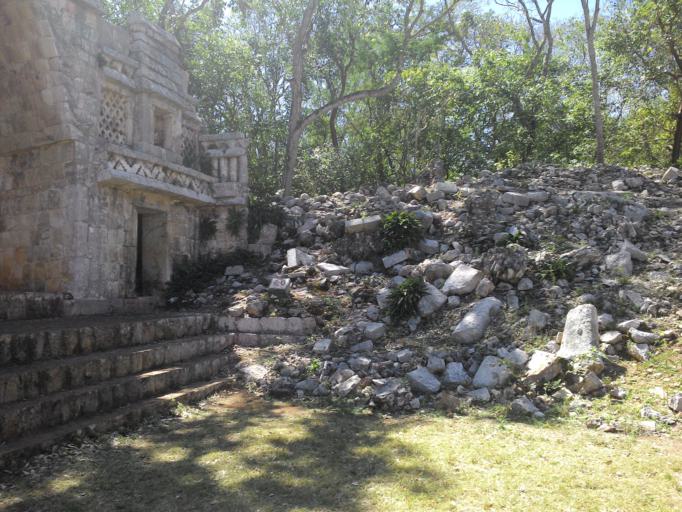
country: MX
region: Yucatan
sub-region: Oxkutzcab
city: Xul
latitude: 20.1713
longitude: -89.5789
